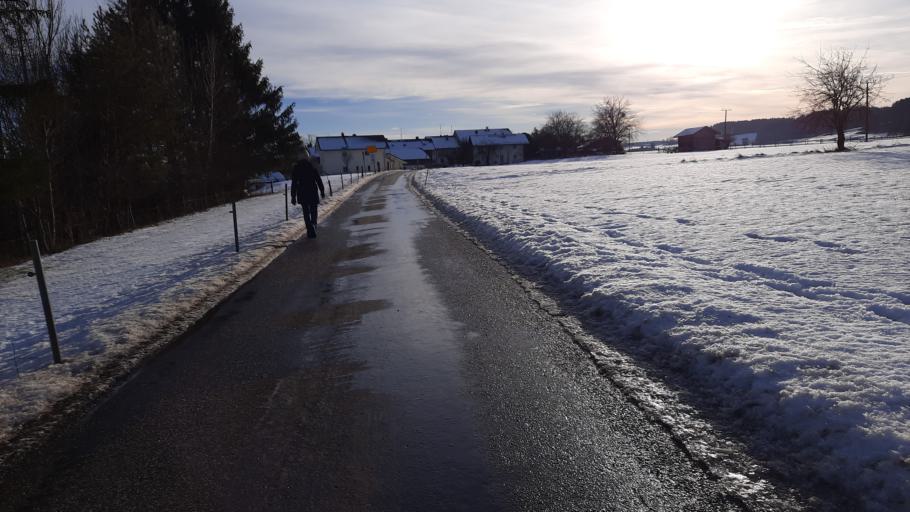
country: DE
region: Bavaria
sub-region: Upper Bavaria
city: Glonn
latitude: 48.0034
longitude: 11.8678
